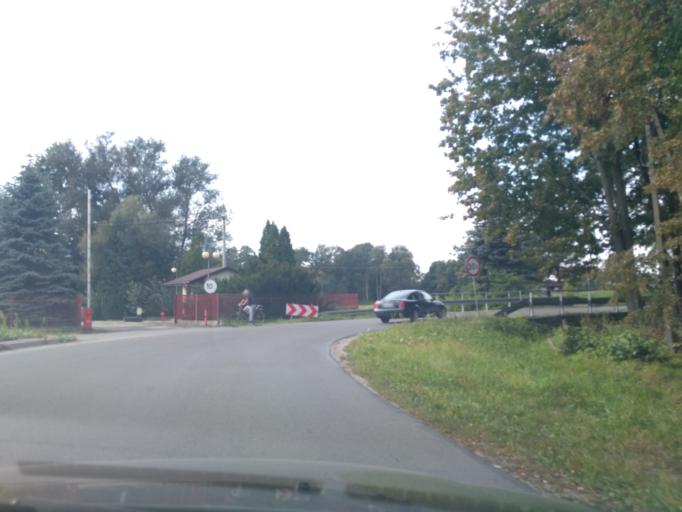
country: PL
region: Subcarpathian Voivodeship
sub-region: Powiat rzeszowski
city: Swilcza
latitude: 50.0923
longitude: 21.9186
